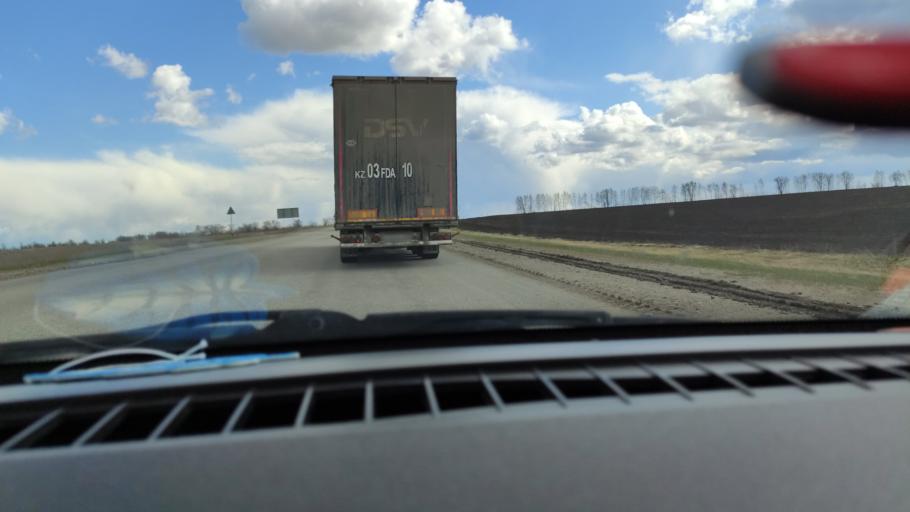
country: RU
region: Samara
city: Varlamovo
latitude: 53.1123
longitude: 48.3527
